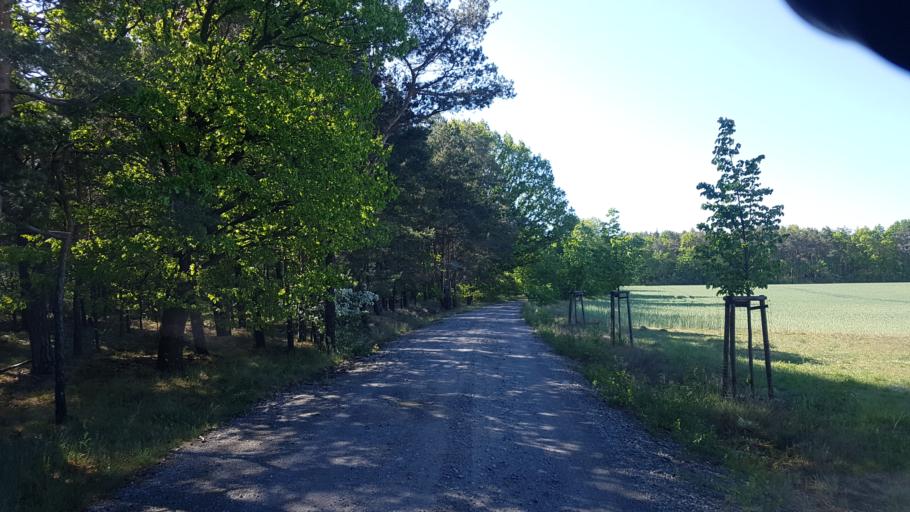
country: DE
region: Brandenburg
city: Grossraschen
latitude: 51.5885
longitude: 13.9620
